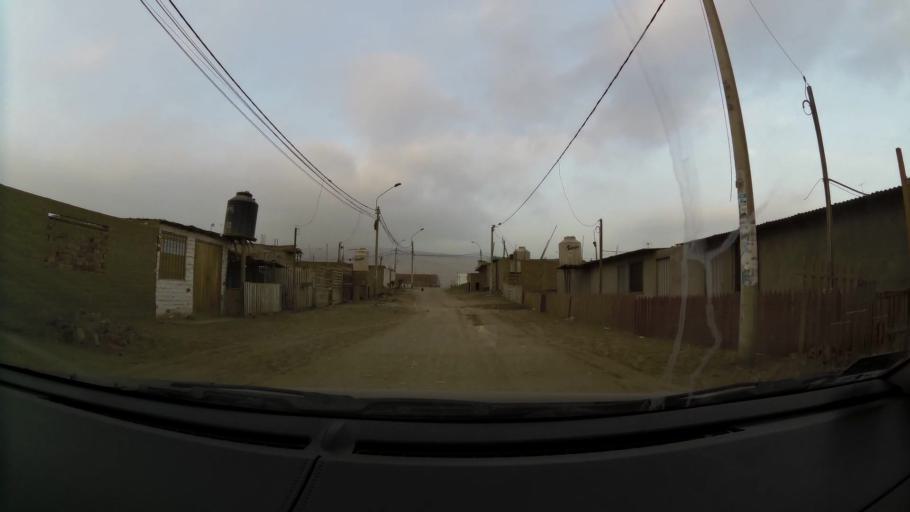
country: PE
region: Lima
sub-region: Lima
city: Santa Rosa
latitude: -11.7337
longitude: -77.1427
